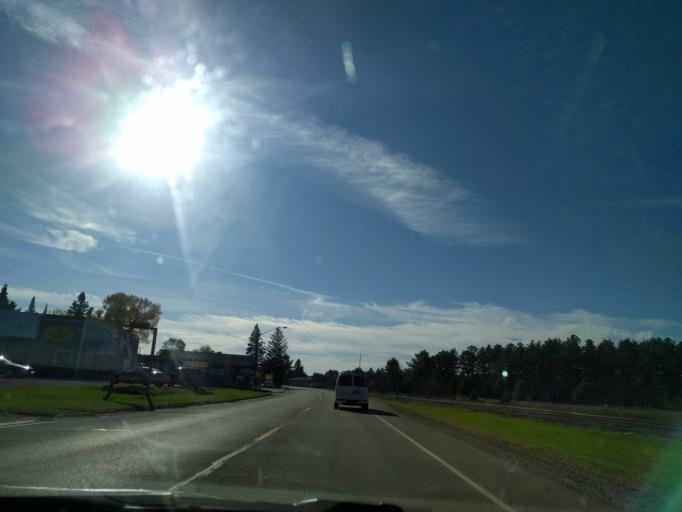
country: US
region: Wisconsin
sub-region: Marinette County
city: Niagara
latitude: 45.6366
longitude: -87.9872
